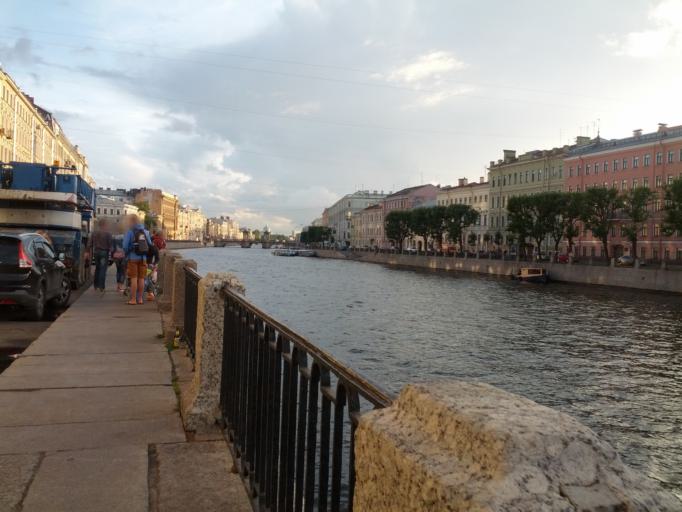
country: RU
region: St.-Petersburg
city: Centralniy
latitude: 59.9311
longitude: 30.3422
